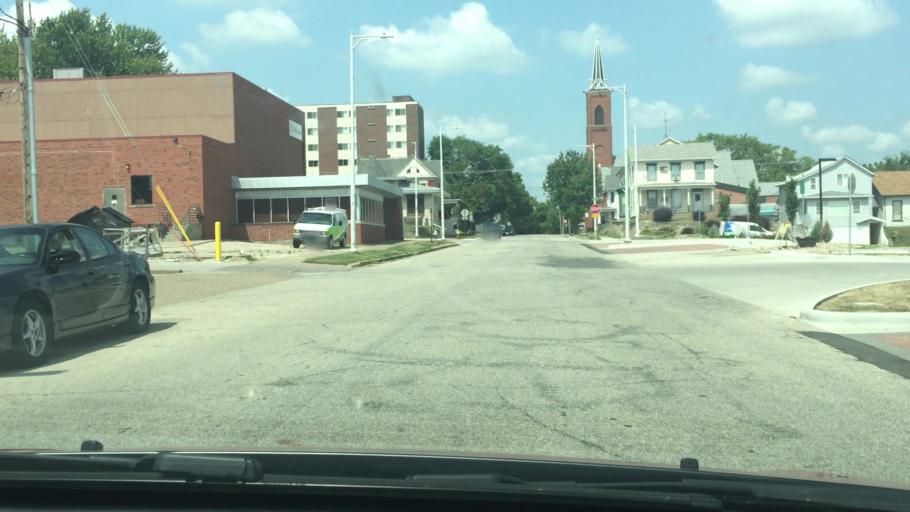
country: US
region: Iowa
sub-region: Muscatine County
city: Muscatine
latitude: 41.4243
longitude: -91.0469
